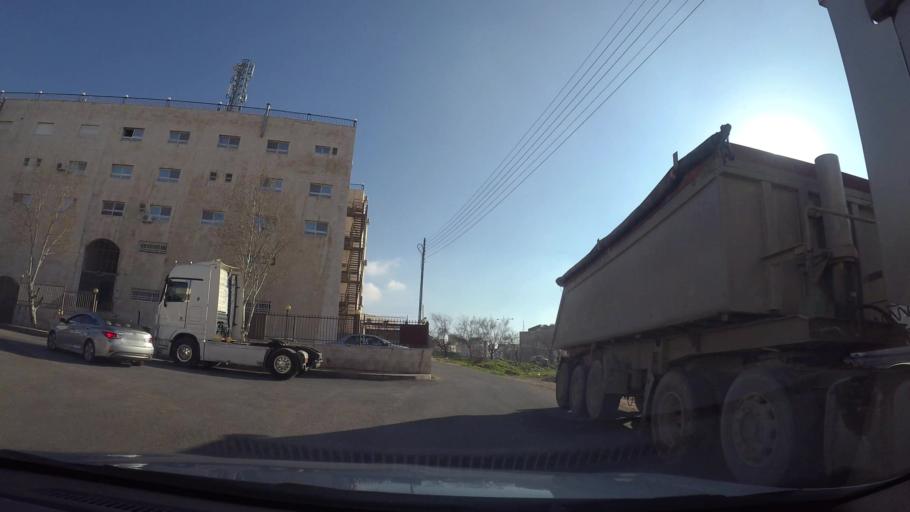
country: JO
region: Amman
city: Al Quwaysimah
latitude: 31.9014
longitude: 35.9272
